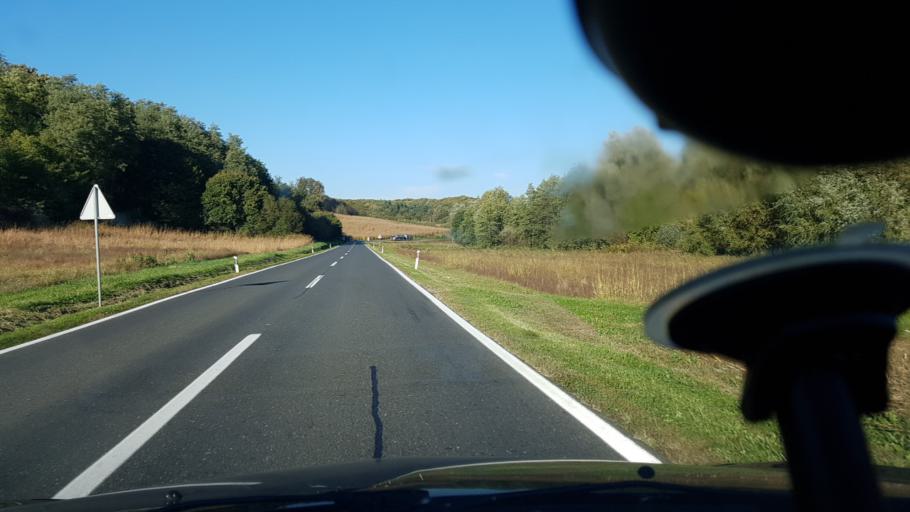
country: HR
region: Koprivnicko-Krizevacka
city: Virje
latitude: 46.0074
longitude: 16.9263
